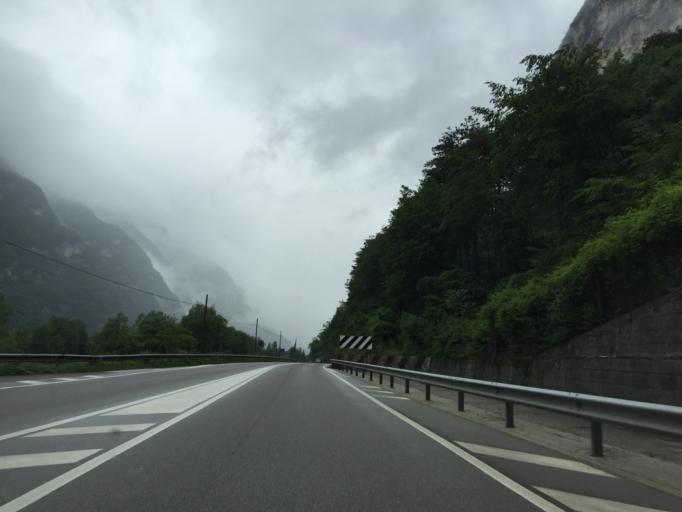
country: IT
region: Trentino-Alto Adige
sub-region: Provincia di Trento
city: Grigno
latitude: 46.0198
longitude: 11.6063
